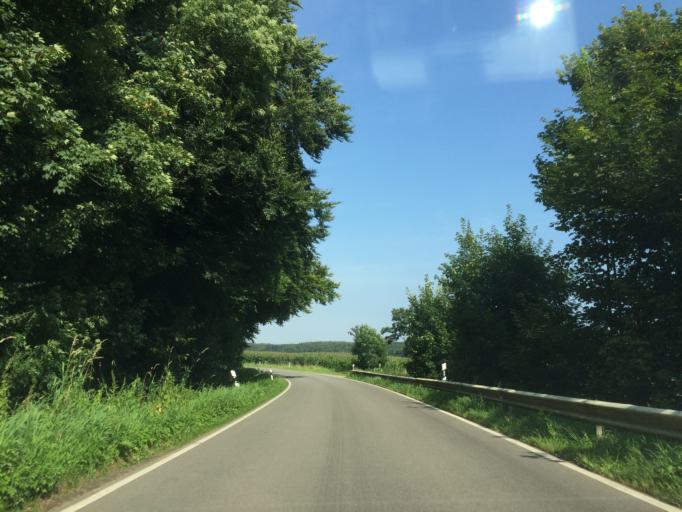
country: DE
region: Schleswig-Holstein
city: Altenhof
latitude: 54.4294
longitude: 9.8933
